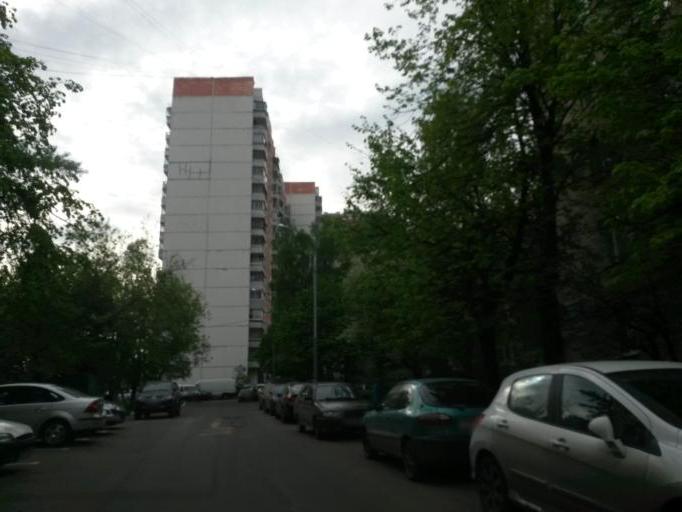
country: RU
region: Moscow
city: Annino
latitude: 55.5633
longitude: 37.5804
